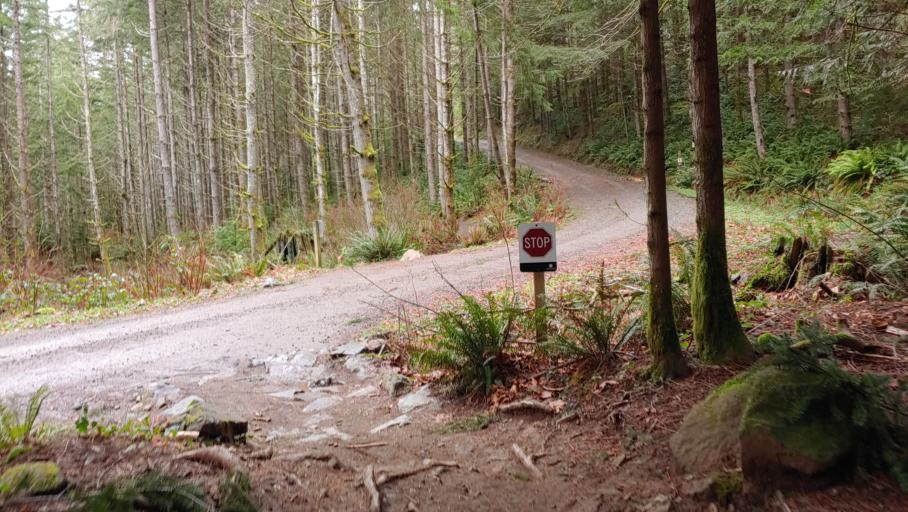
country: US
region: Washington
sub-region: King County
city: Hobart
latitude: 47.4687
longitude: -121.9306
